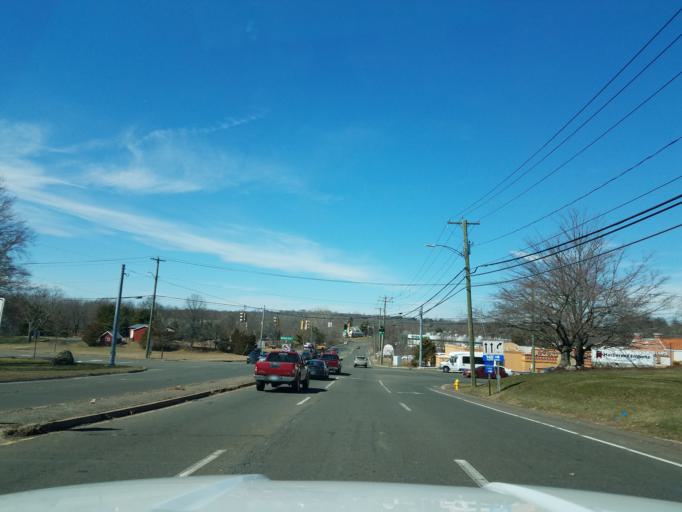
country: US
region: Connecticut
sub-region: New Haven County
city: Orange
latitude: 41.2593
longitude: -73.0015
